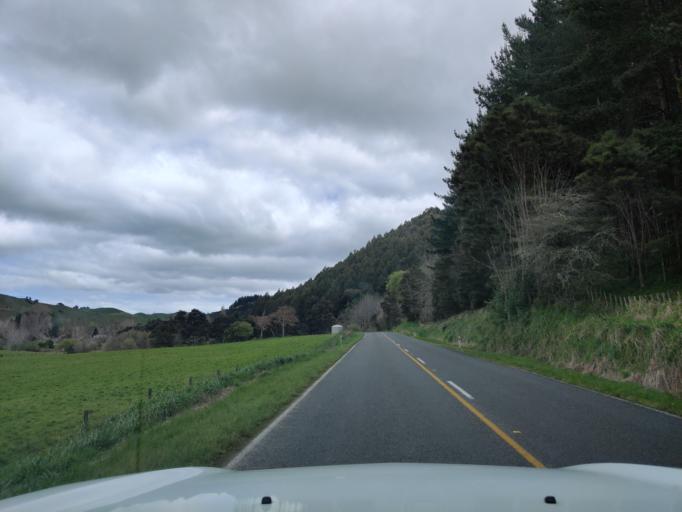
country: NZ
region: Manawatu-Wanganui
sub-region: Wanganui District
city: Wanganui
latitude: -39.8345
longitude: 175.1616
